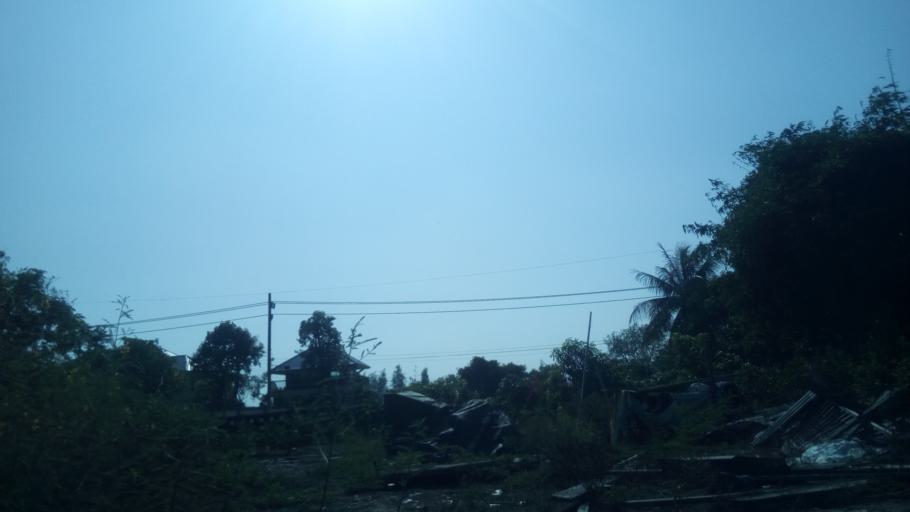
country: TH
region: Nakhon Pathom
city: Salaya
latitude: 13.8079
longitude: 100.3091
